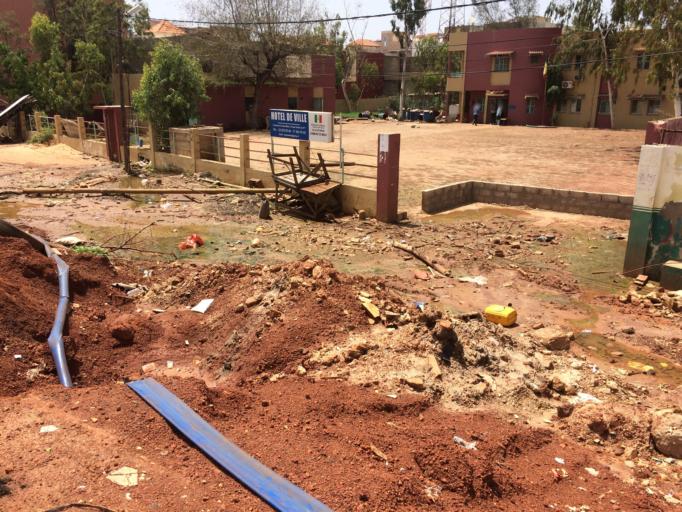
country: SN
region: Dakar
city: Pikine
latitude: 14.7387
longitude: -17.3110
